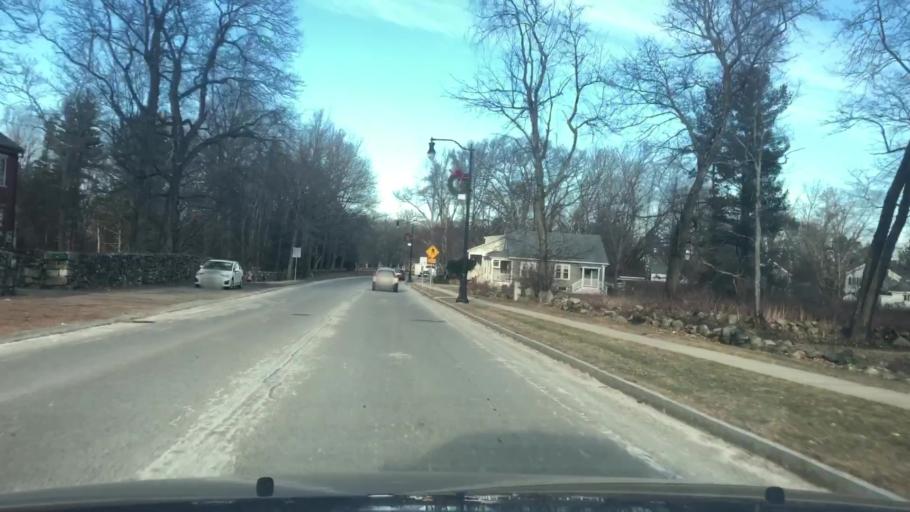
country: US
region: Massachusetts
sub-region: Essex County
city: North Andover
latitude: 42.6818
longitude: -71.1172
